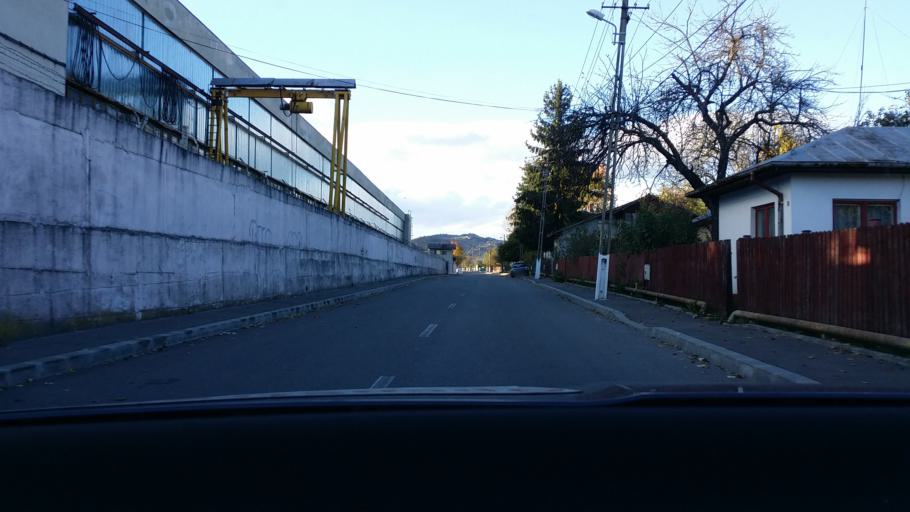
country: RO
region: Prahova
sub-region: Municipiul Campina
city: Campina
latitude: 45.1350
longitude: 25.7425
